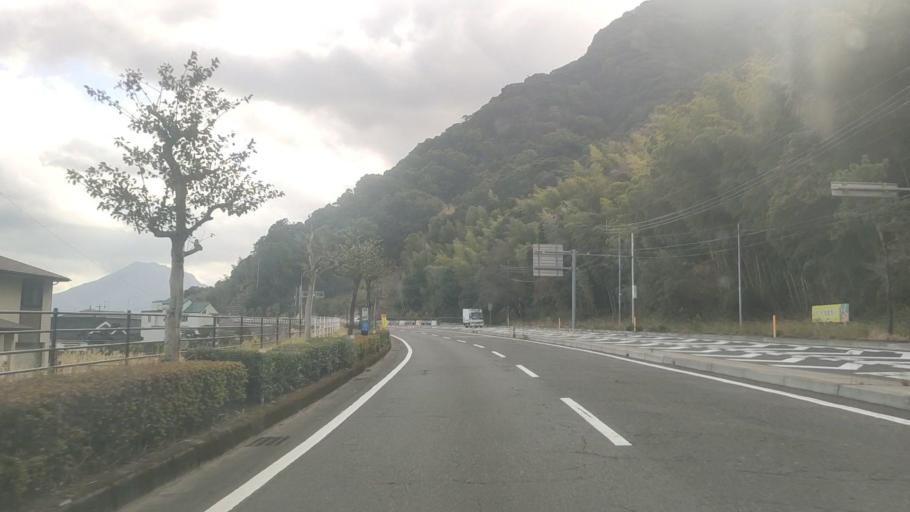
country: JP
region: Kagoshima
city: Kajiki
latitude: 31.7023
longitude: 130.6115
